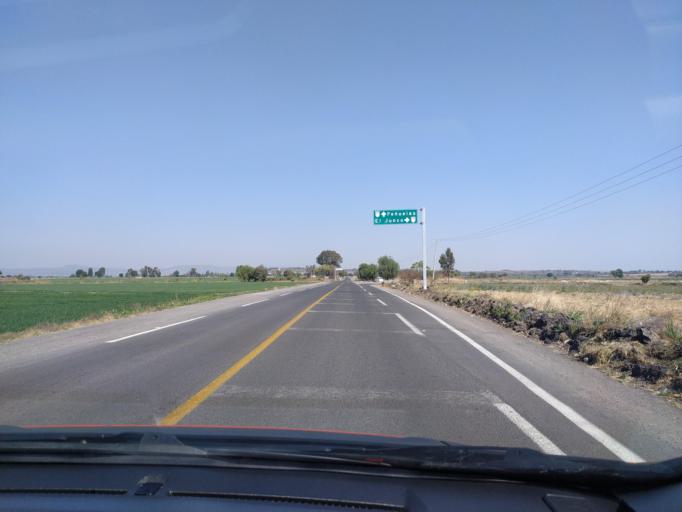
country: MX
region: Guanajuato
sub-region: San Francisco del Rincon
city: San Ignacio de Hidalgo
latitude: 20.8364
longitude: -101.8459
